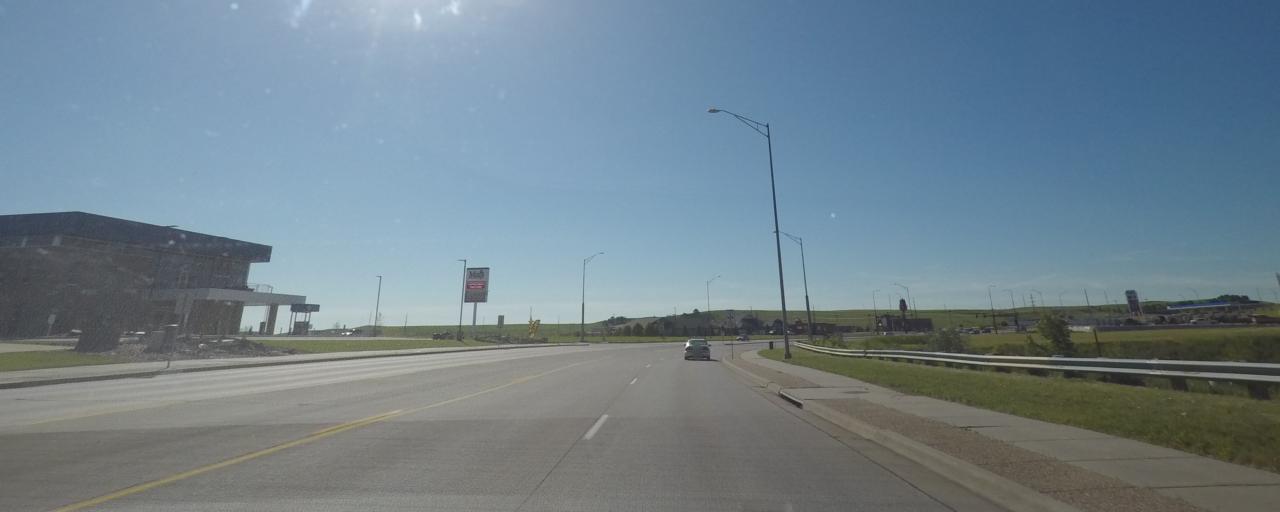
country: US
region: South Dakota
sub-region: Pennington County
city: Rapid City
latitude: 44.0348
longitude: -103.2142
